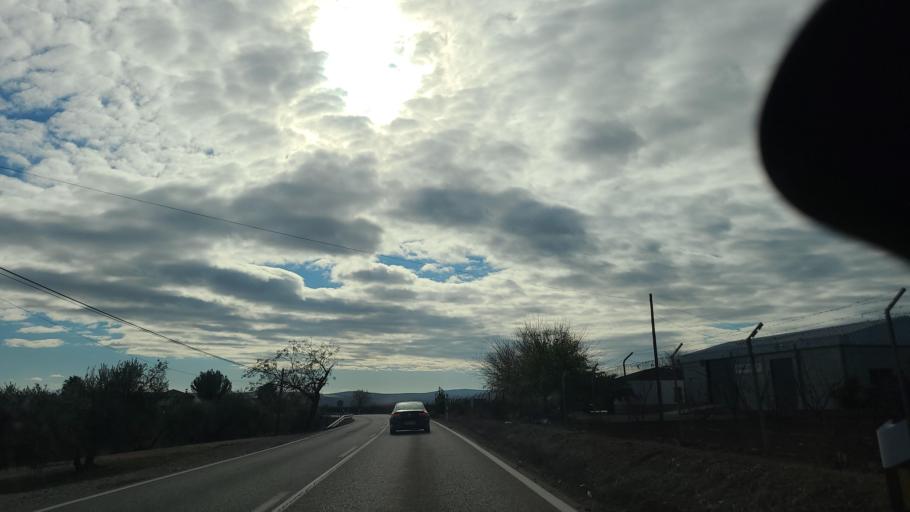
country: ES
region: Andalusia
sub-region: Provincia de Jaen
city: Villanueva de la Reina
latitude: 38.0390
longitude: -3.9152
